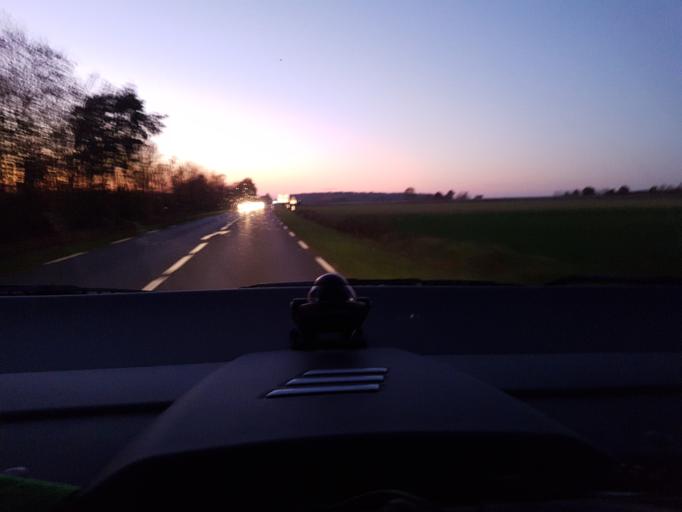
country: FR
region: Picardie
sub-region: Departement de la Somme
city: Saint-Valery-sur-Somme
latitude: 50.1745
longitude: 1.6186
